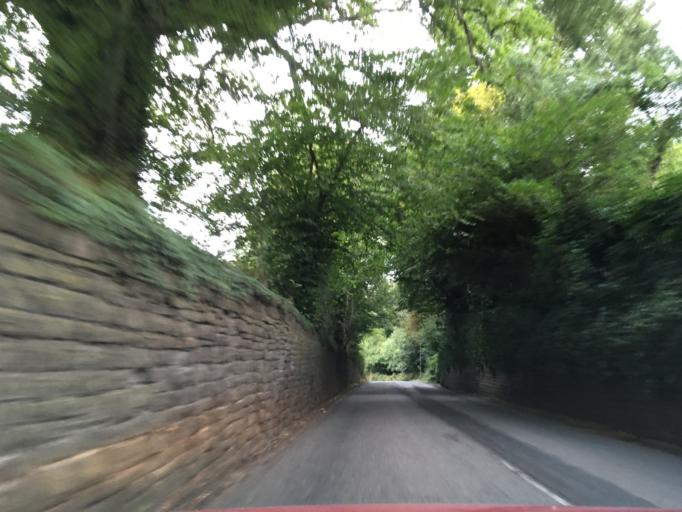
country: GB
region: England
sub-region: Wiltshire
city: Bremhill
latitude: 51.4355
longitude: -2.0653
